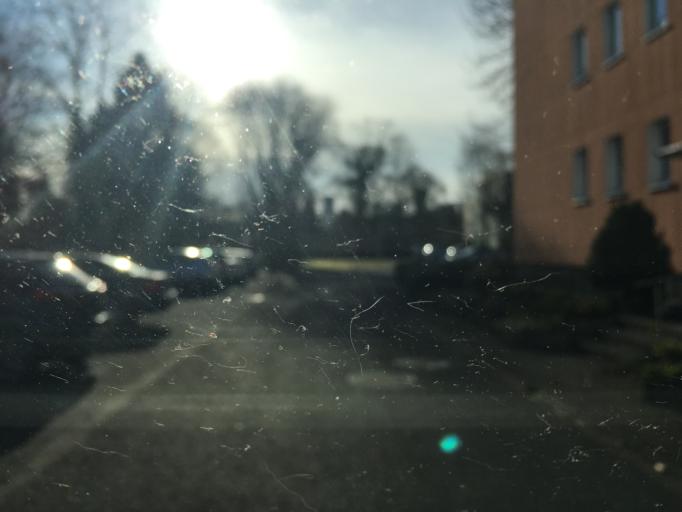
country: DE
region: North Rhine-Westphalia
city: Bruhl
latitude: 50.8294
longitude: 6.8878
